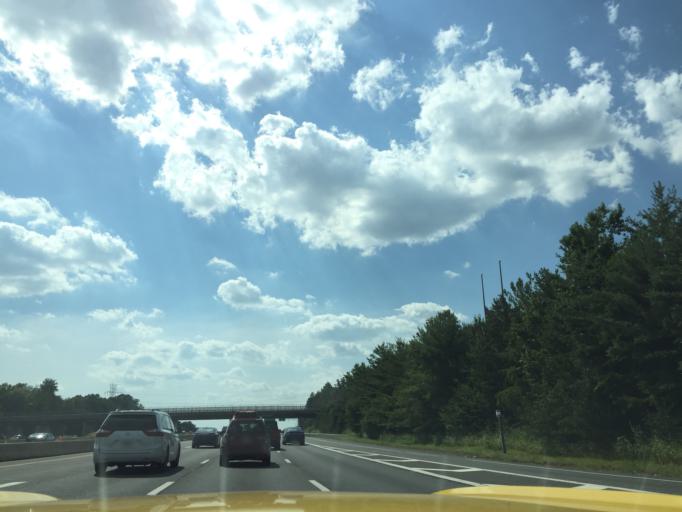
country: US
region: Virginia
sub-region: Fairfax County
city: Herndon
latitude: 38.9532
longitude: -77.3860
